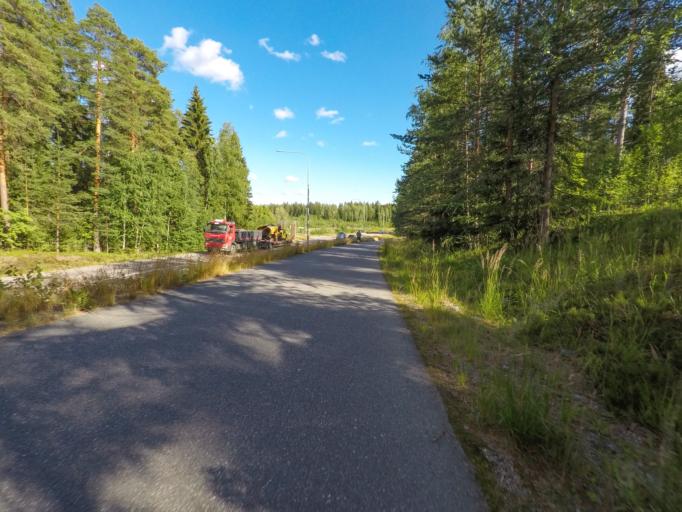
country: FI
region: South Karelia
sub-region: Lappeenranta
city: Lappeenranta
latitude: 61.0971
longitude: 28.1357
